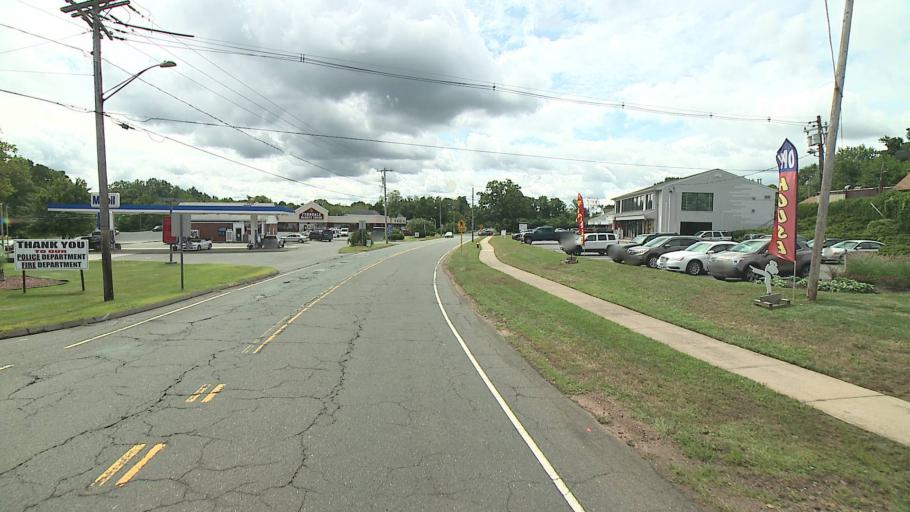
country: US
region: Connecticut
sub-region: Hartford County
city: Kensington
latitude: 41.6356
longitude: -72.7884
